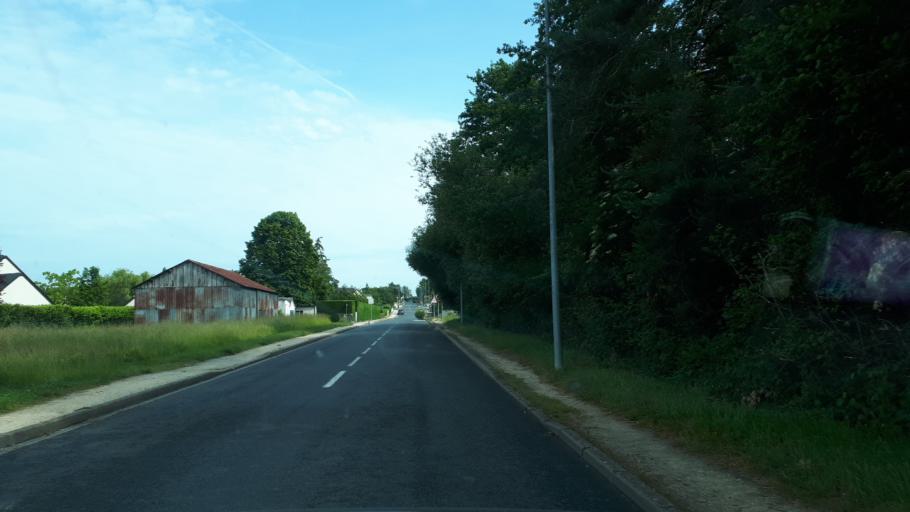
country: FR
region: Centre
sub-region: Departement d'Indre-et-Loire
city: Monnaie
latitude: 47.5061
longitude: 0.7934
